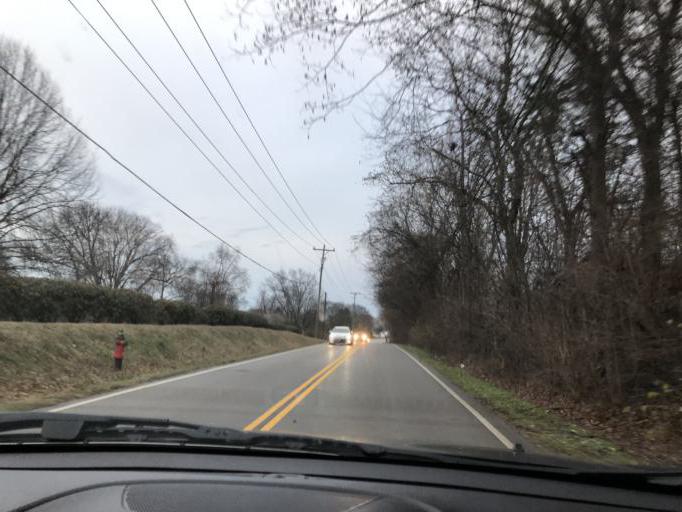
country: US
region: Tennessee
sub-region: Wilson County
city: Green Hill
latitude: 36.1888
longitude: -86.5885
